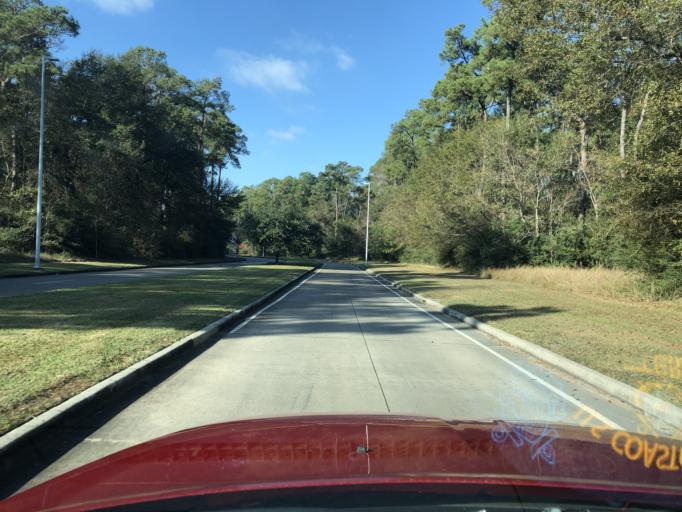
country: US
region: Texas
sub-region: Harris County
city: Aldine
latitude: 29.9727
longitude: -95.3356
